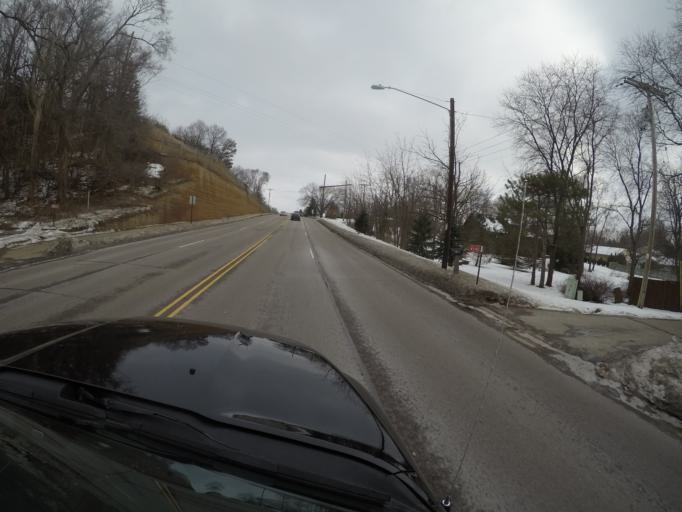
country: US
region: Wisconsin
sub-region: La Crosse County
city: Onalaska
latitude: 43.8805
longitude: -91.2043
